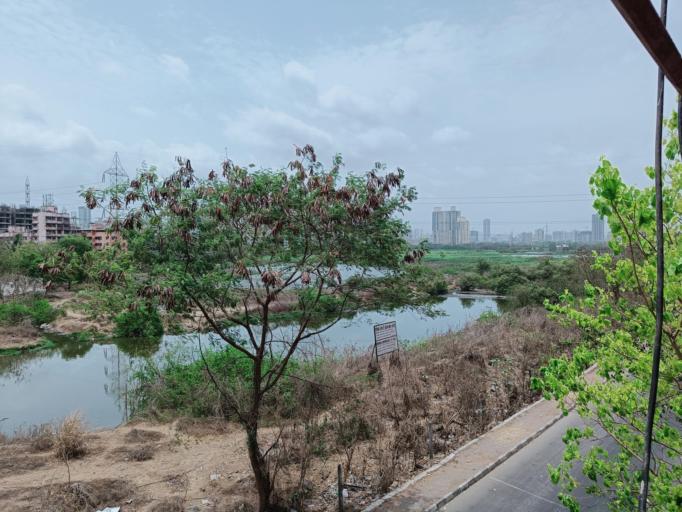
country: IN
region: Maharashtra
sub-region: Thane
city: Airoli
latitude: 19.1466
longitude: 72.9488
